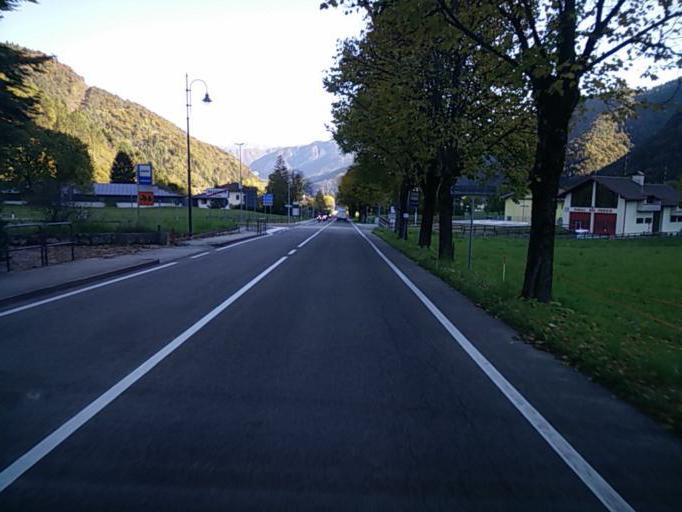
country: IT
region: Trentino-Alto Adige
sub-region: Provincia di Trento
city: Pieve di Ledro
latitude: 45.8935
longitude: 10.7234
